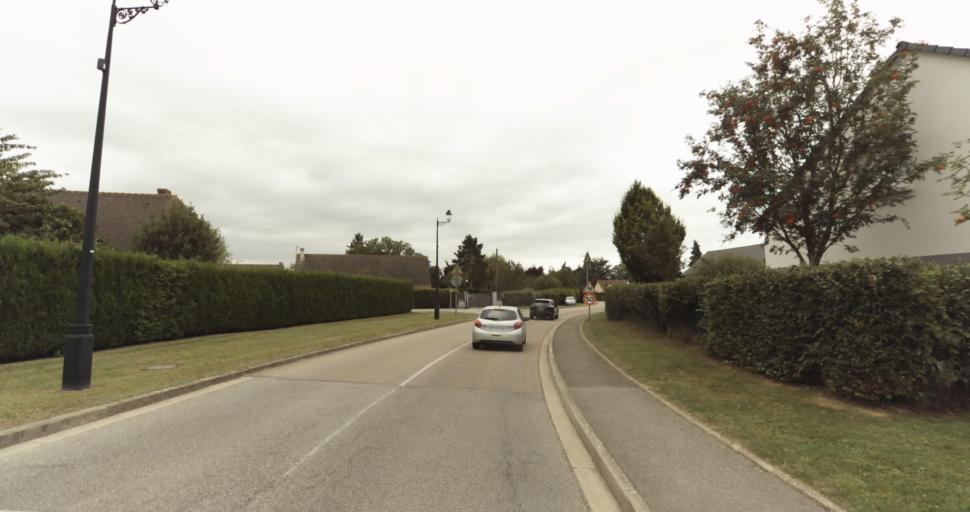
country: FR
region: Haute-Normandie
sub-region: Departement de l'Eure
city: Gravigny
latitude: 49.0392
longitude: 1.2103
